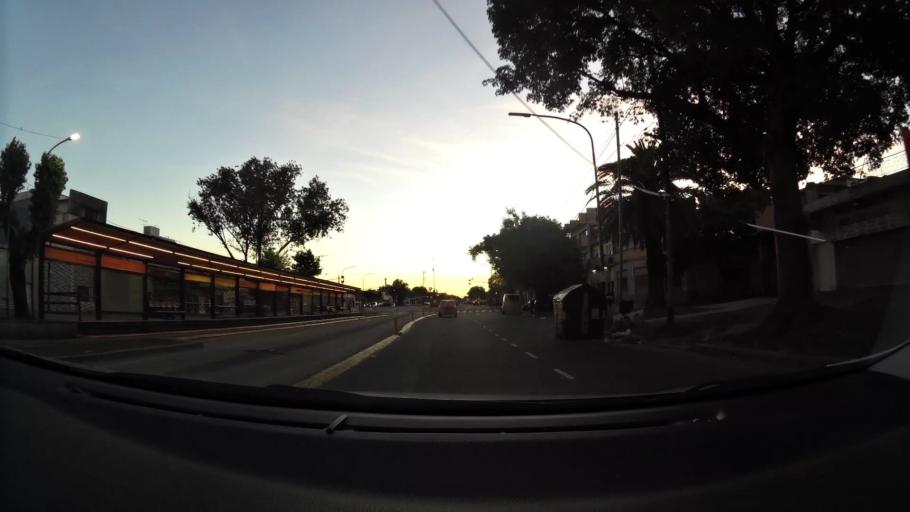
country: AR
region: Buenos Aires F.D.
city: Villa Lugano
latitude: -34.6493
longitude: -58.4300
